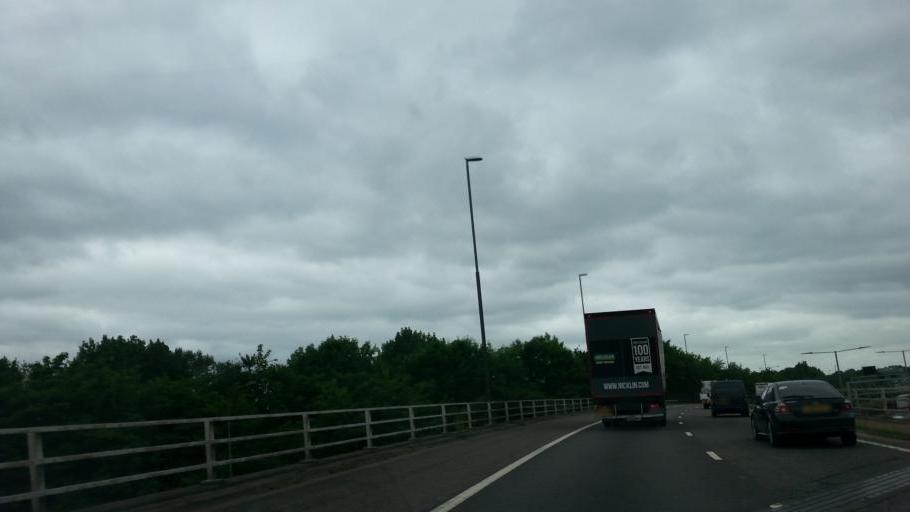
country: GB
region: England
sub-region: Warwickshire
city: Water Orton
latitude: 52.5074
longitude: -1.7439
